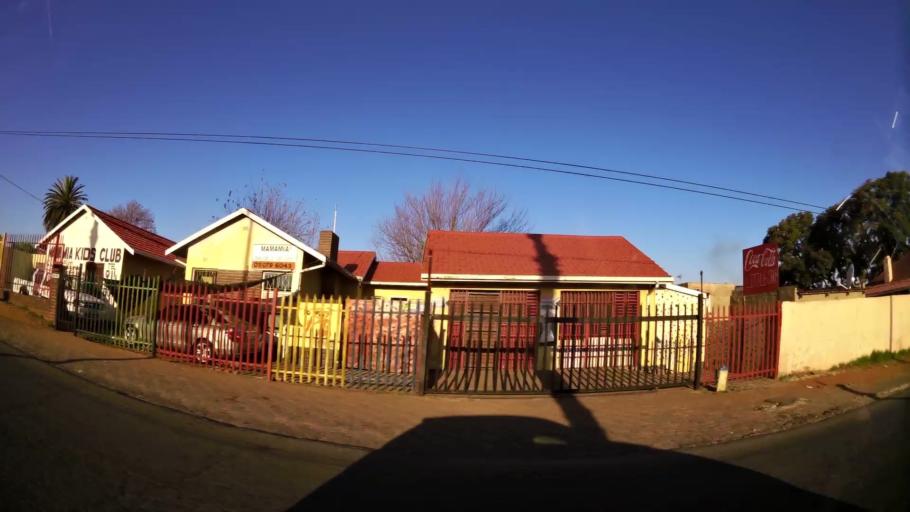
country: ZA
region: Gauteng
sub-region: City of Johannesburg Metropolitan Municipality
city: Roodepoort
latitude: -26.1601
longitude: 27.8740
